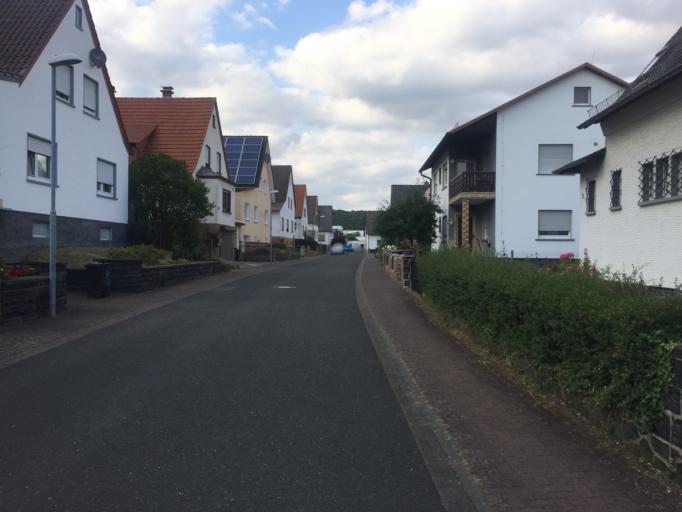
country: DE
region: Hesse
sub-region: Regierungsbezirk Giessen
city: Heuchelheim
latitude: 50.6440
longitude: 8.5955
